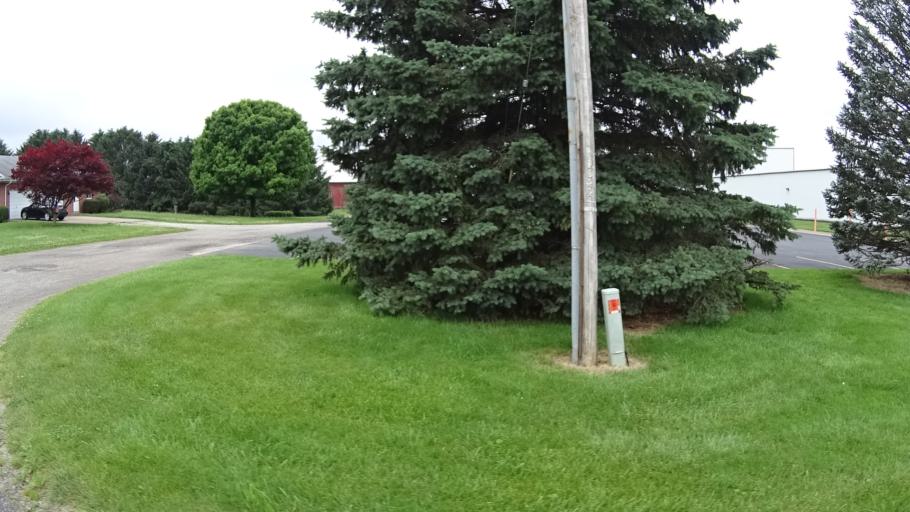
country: US
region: Ohio
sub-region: Erie County
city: Milan
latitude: 41.3124
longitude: -82.5432
